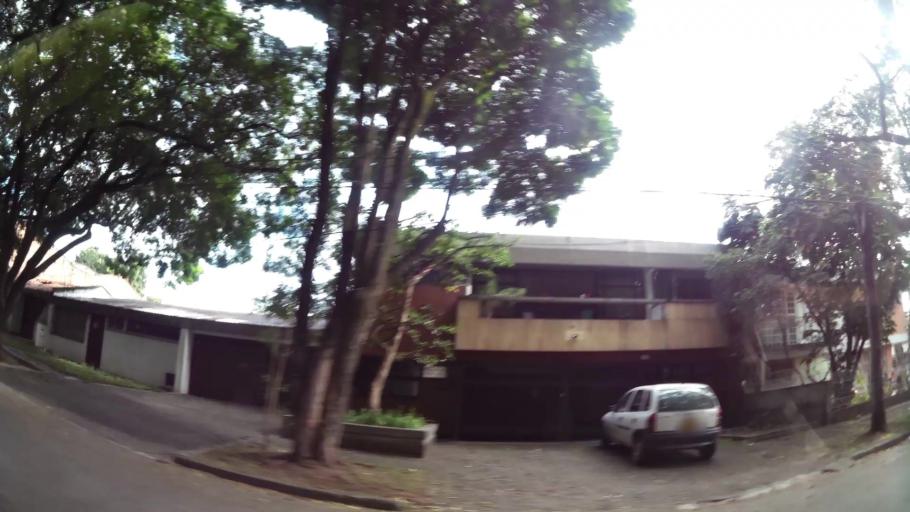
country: CO
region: Valle del Cauca
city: Cali
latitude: 3.4828
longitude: -76.5241
